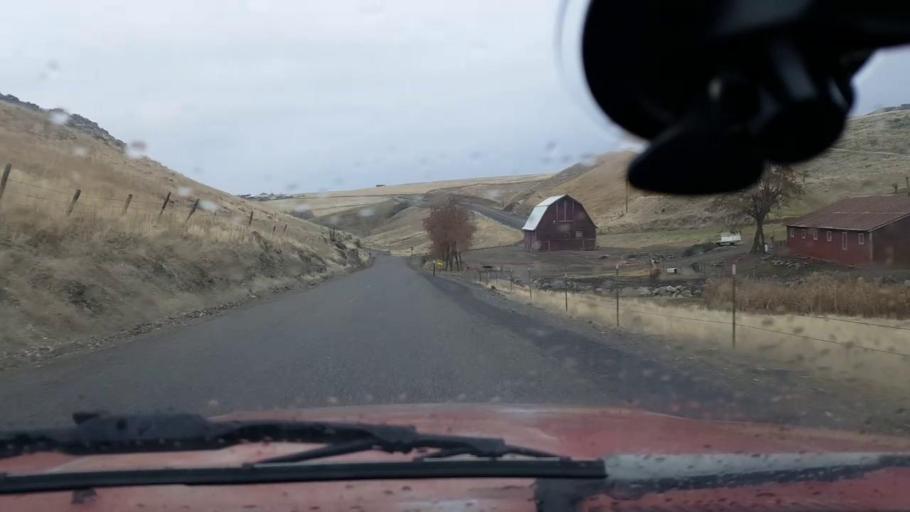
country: US
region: Washington
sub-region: Asotin County
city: Clarkston Heights-Vineland
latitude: 46.3880
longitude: -117.1393
